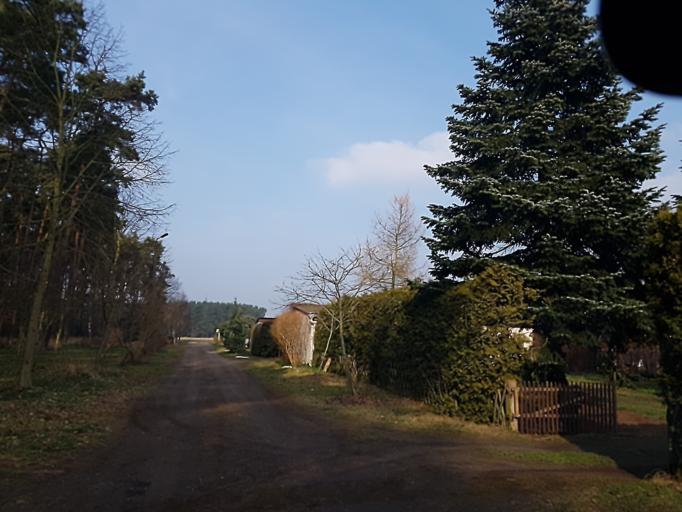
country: DE
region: Brandenburg
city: Wollin
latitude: 52.2848
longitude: 12.4657
